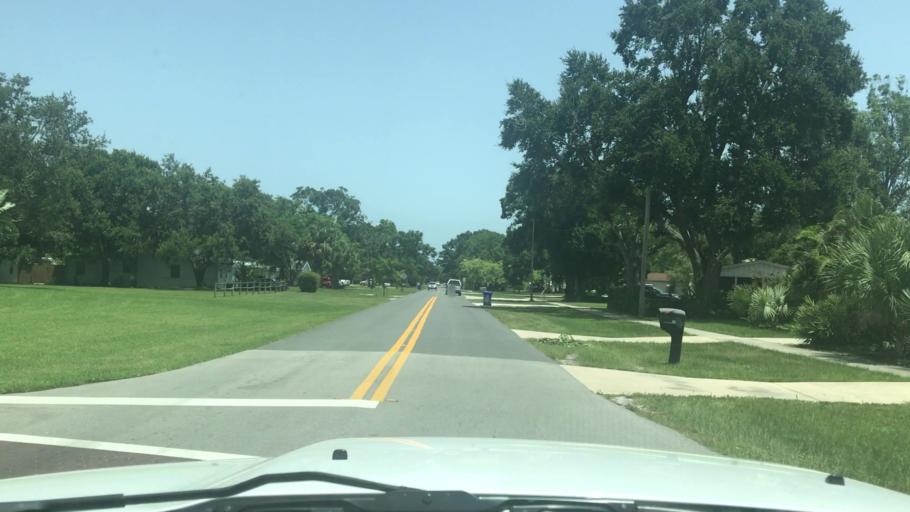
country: US
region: Florida
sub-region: Indian River County
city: Vero Beach
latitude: 27.6418
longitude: -80.4203
